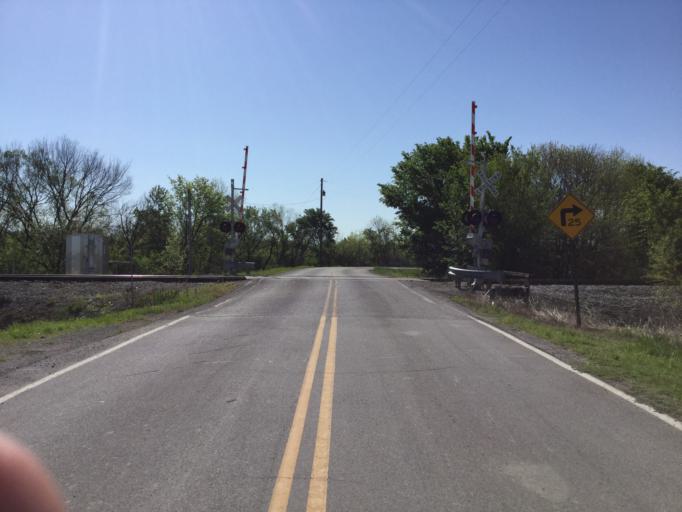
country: US
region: Kansas
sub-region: Montgomery County
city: Cherryvale
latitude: 37.3108
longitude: -95.5391
